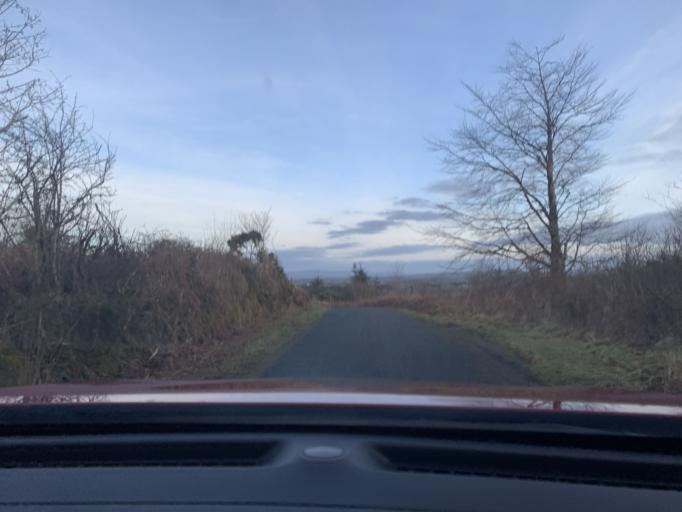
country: IE
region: Connaught
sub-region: Sligo
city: Strandhill
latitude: 54.1771
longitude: -8.6331
